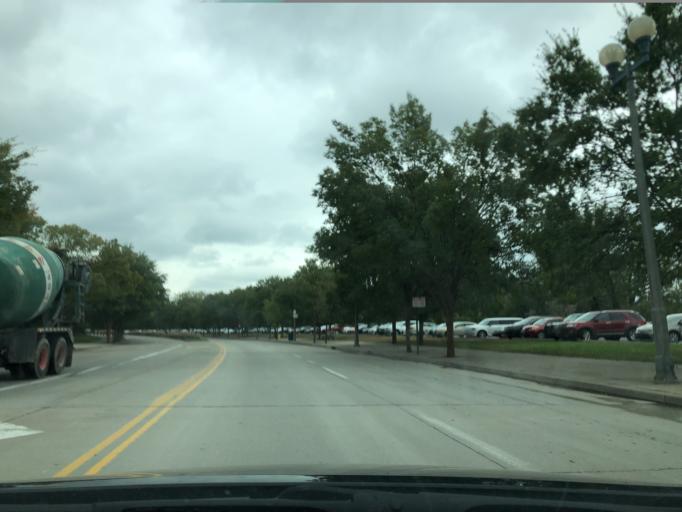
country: US
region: Kentucky
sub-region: Kenton County
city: Covington
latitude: 39.0942
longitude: -84.5179
